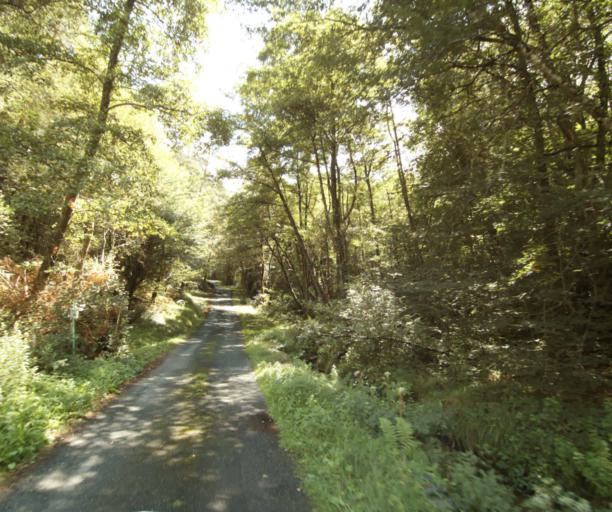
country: FR
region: Limousin
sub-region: Departement de la Correze
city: Sainte-Fortunade
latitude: 45.2144
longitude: 1.8030
